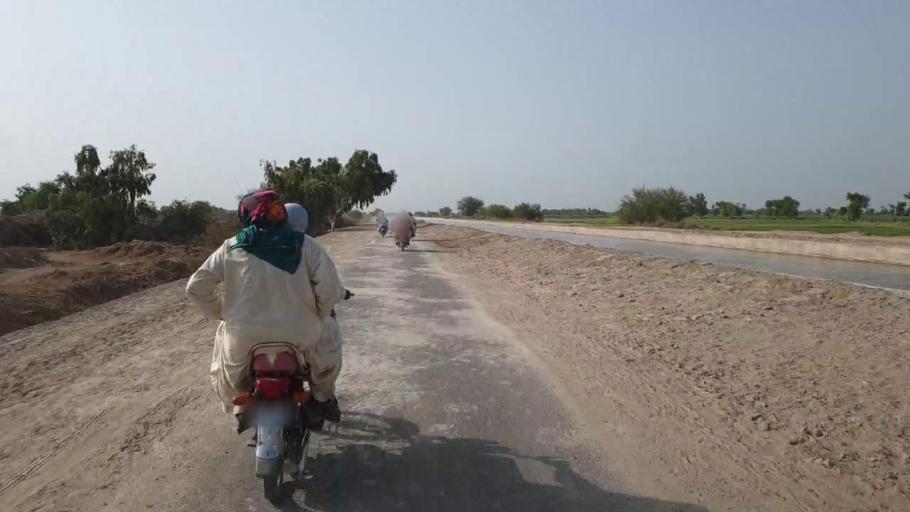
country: PK
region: Sindh
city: Daur
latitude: 26.3404
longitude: 68.1630
